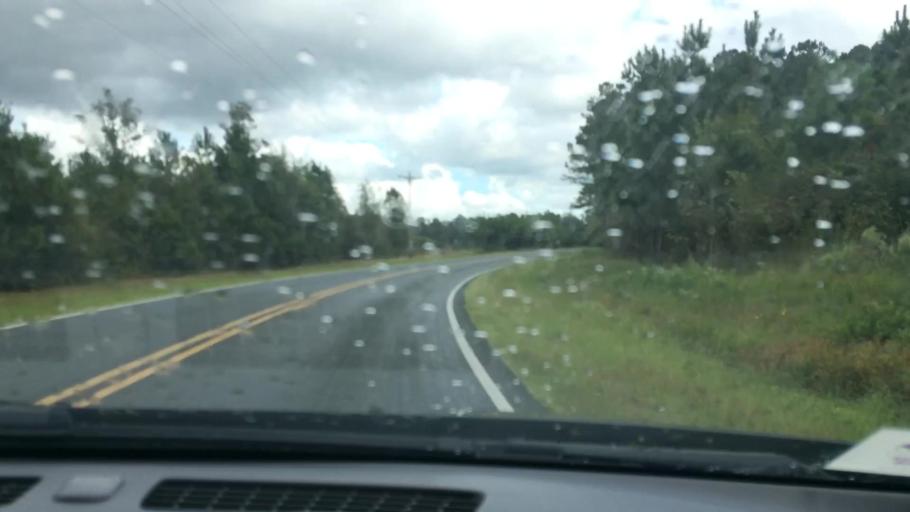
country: US
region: North Carolina
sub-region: Greene County
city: Maury
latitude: 35.5208
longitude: -77.5377
